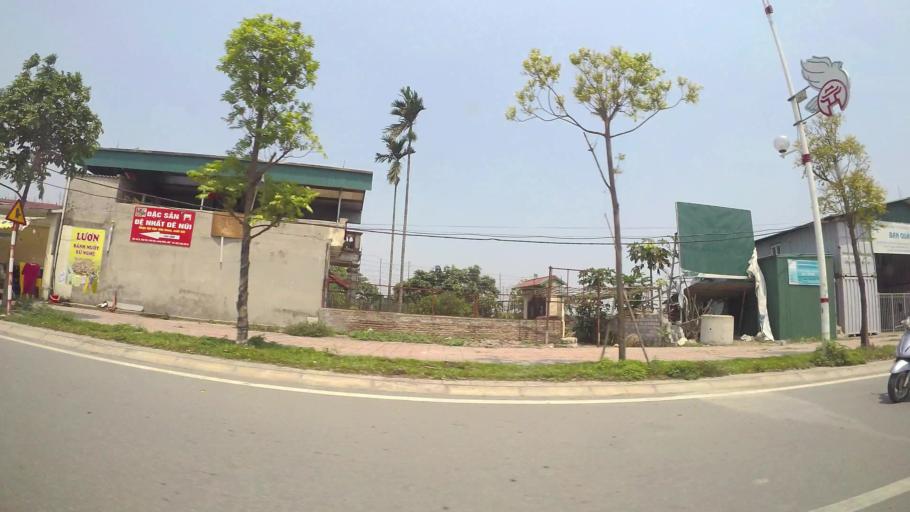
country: VN
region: Ha Noi
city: Hoan Kiem
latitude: 21.0348
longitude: 105.8801
